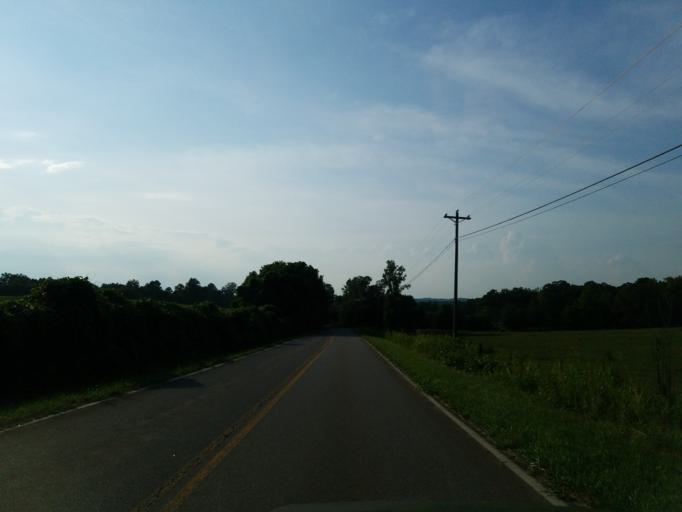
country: US
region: Georgia
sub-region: Pickens County
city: Jasper
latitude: 34.5382
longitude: -84.5345
